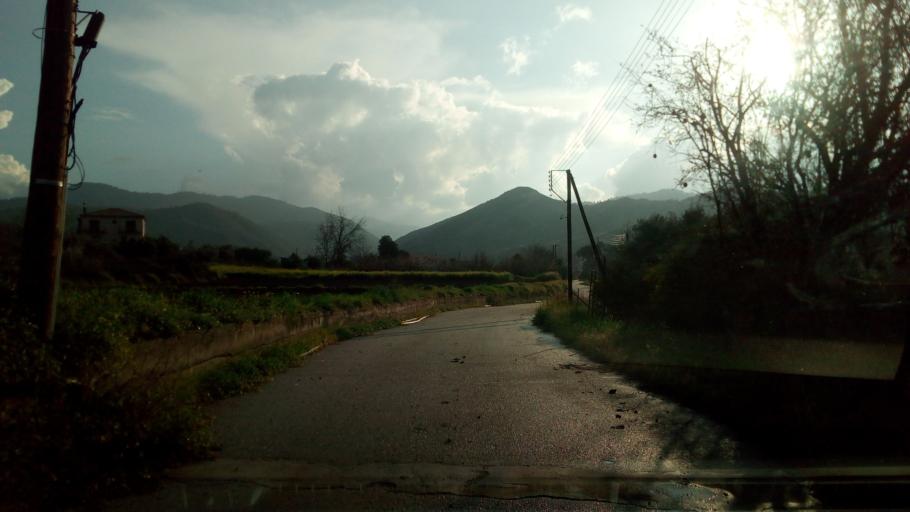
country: CY
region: Lefkosia
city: Kato Pyrgos
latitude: 35.1767
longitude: 32.6775
